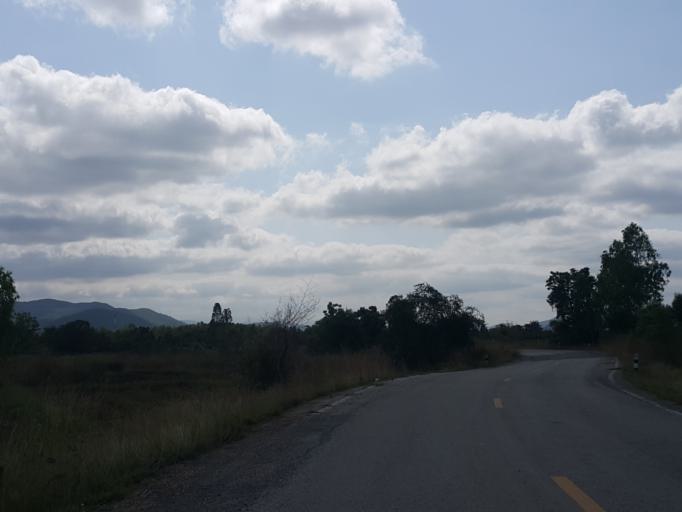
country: TH
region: Lamphun
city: Lamphun
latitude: 18.5388
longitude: 99.0871
